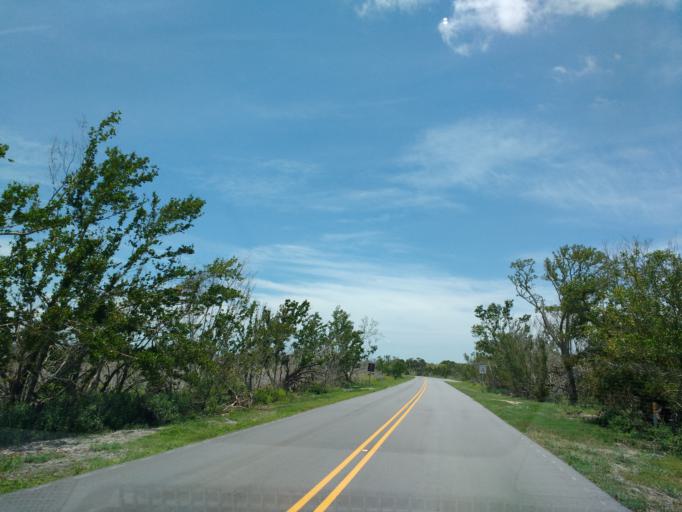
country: US
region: Florida
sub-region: Monroe County
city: Islamorada
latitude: 25.1388
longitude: -80.9358
